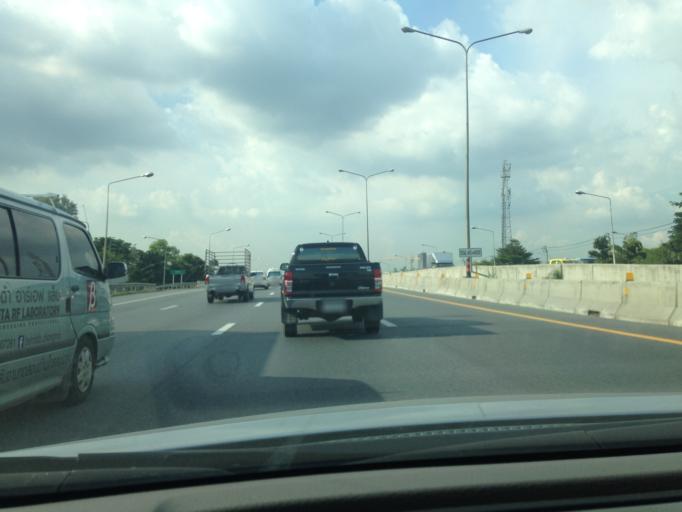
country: TH
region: Bangkok
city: Bueng Kum
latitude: 13.8015
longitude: 100.6804
